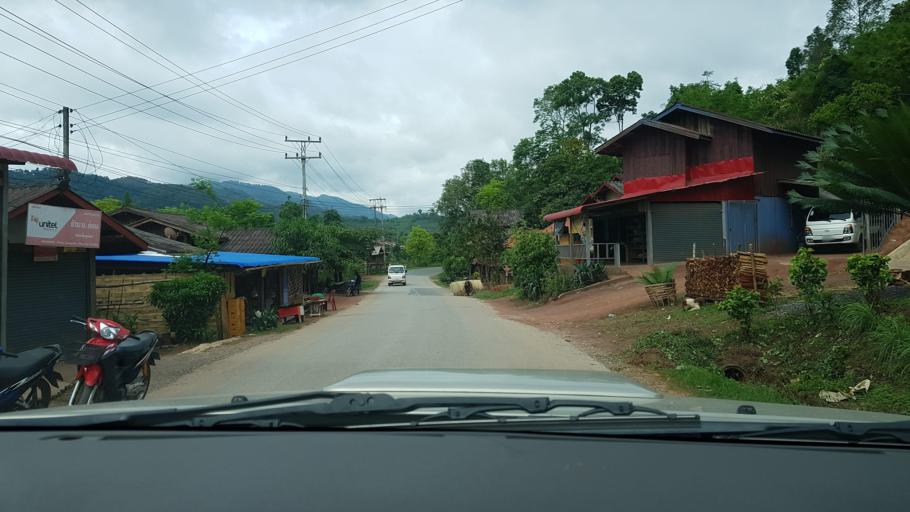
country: LA
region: Oudomxai
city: Muang Xay
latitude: 20.5921
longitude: 101.9340
